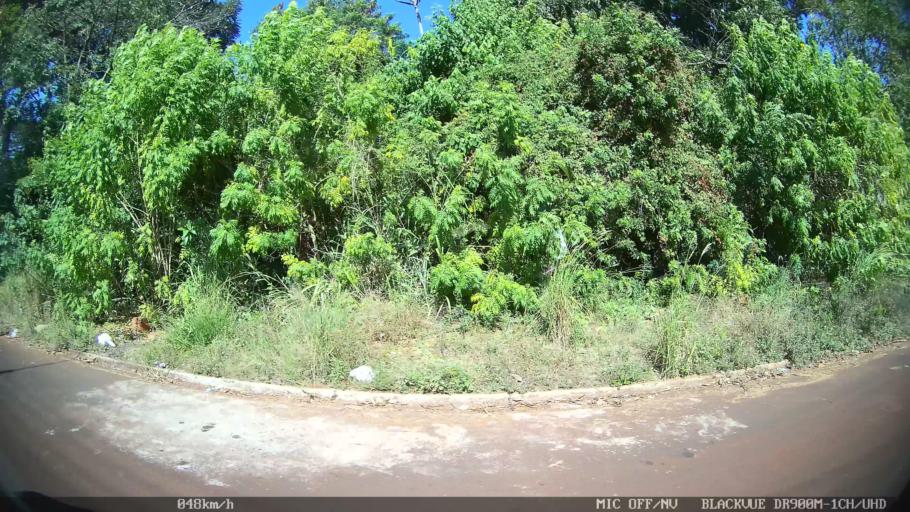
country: BR
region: Sao Paulo
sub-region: Batatais
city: Batatais
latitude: -20.8908
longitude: -47.5771
